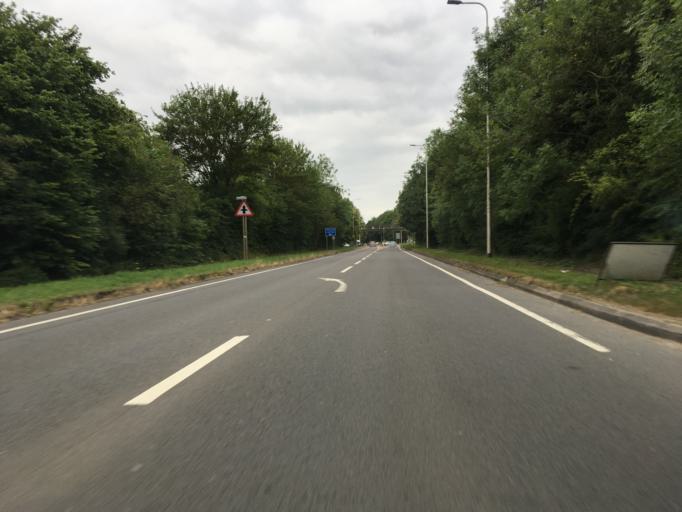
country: GB
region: England
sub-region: Hertfordshire
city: Markyate
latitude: 51.8349
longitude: -0.4554
